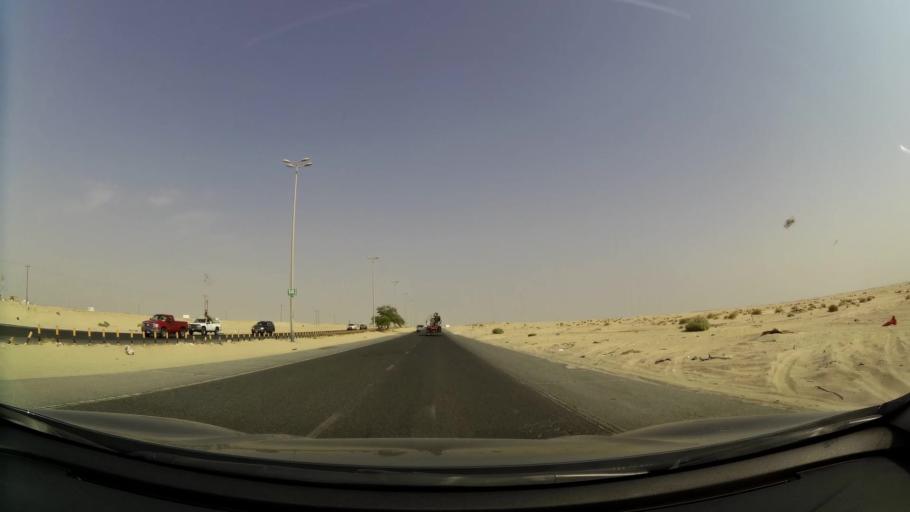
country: KW
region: Al Ahmadi
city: Al Ahmadi
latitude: 28.8406
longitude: 48.0591
